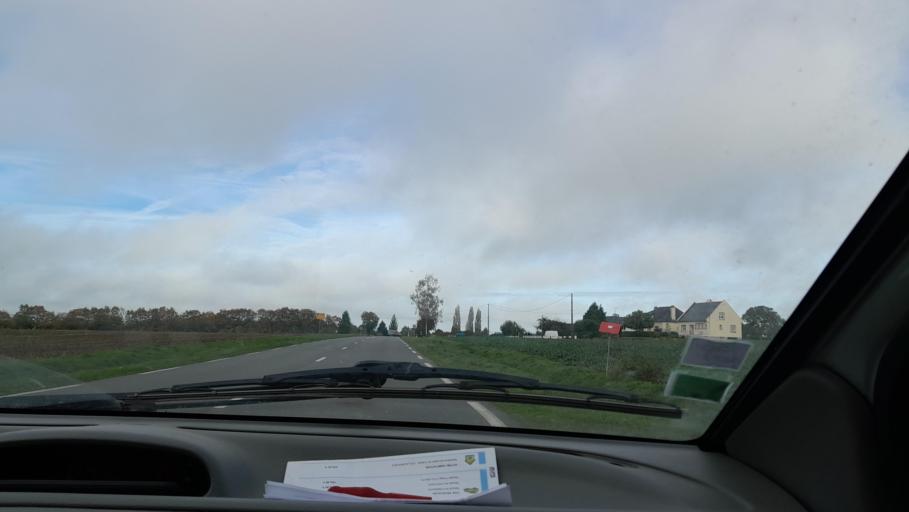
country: FR
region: Brittany
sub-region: Departement d'Ille-et-Vilaine
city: Lecousse
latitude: 48.3690
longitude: -1.2375
